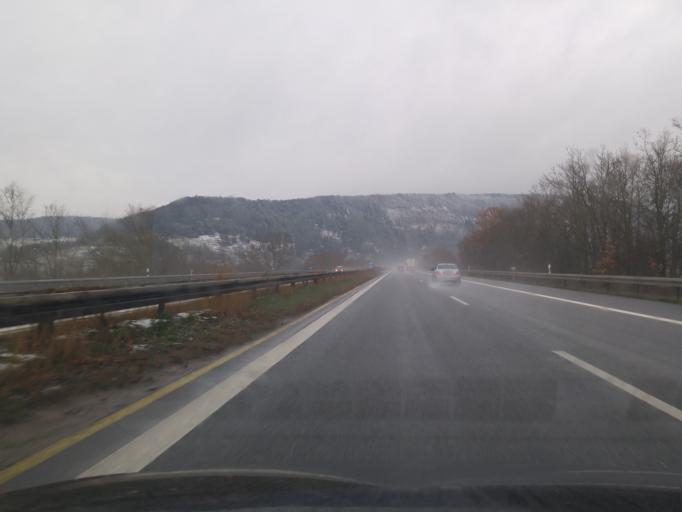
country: DE
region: Bavaria
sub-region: Regierungsbezirk Unterfranken
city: Elfershausen
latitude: 50.1332
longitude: 9.9543
